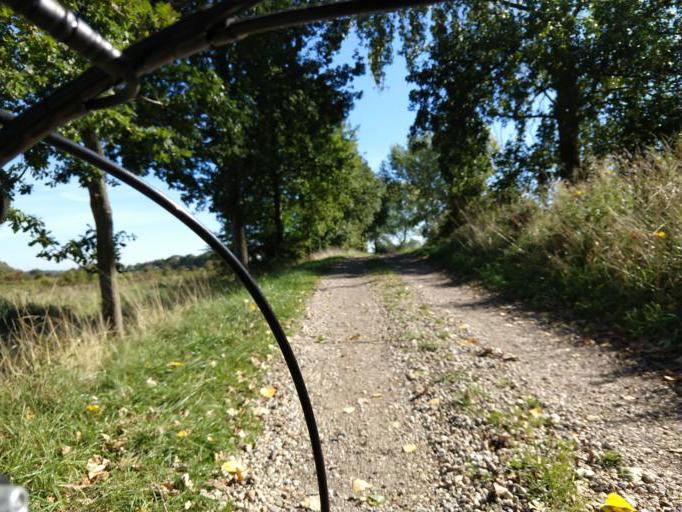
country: NL
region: Zeeland
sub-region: Gemeente Goes
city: Goes
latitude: 51.4443
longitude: 3.8445
